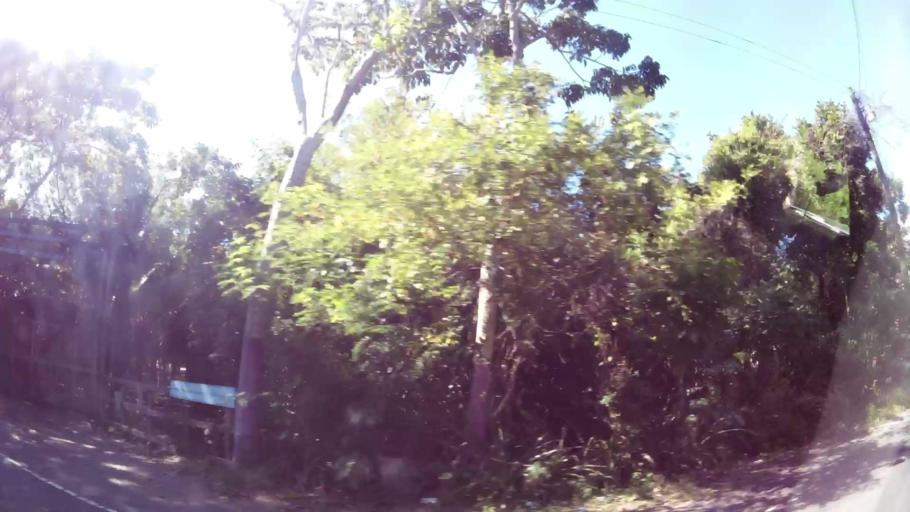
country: GT
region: Santa Rosa
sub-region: Municipio de Taxisco
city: Taxisco
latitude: 13.8914
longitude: -90.4776
